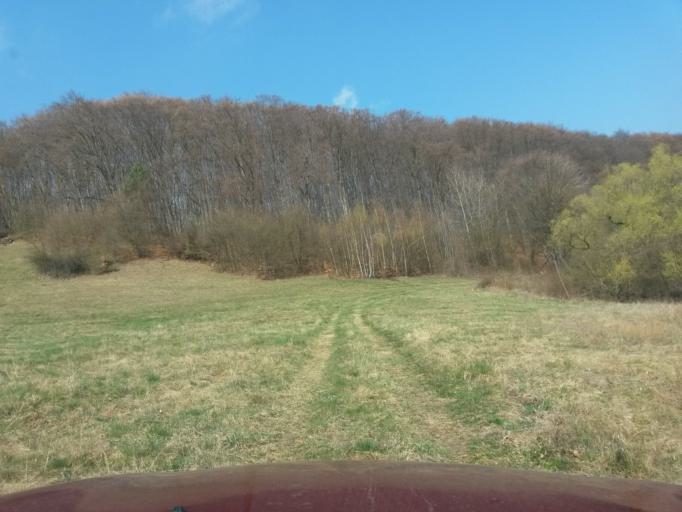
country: SK
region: Presovsky
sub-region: Okres Presov
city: Presov
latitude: 48.9286
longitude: 21.1434
